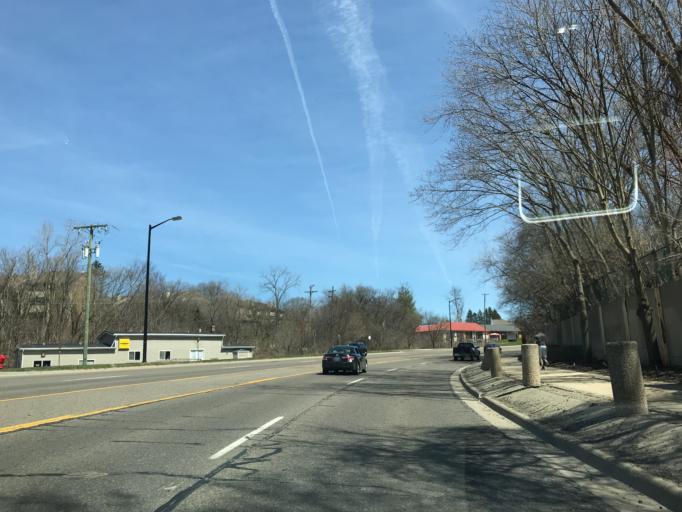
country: US
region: Michigan
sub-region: Washtenaw County
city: Ann Arbor
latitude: 42.2994
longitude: -83.7257
